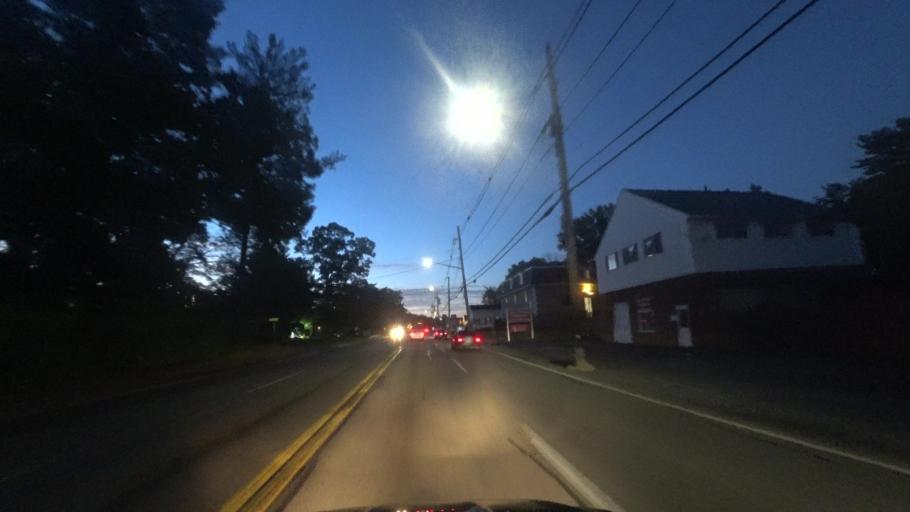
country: US
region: Massachusetts
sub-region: Middlesex County
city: North Reading
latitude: 42.5849
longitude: -71.1141
